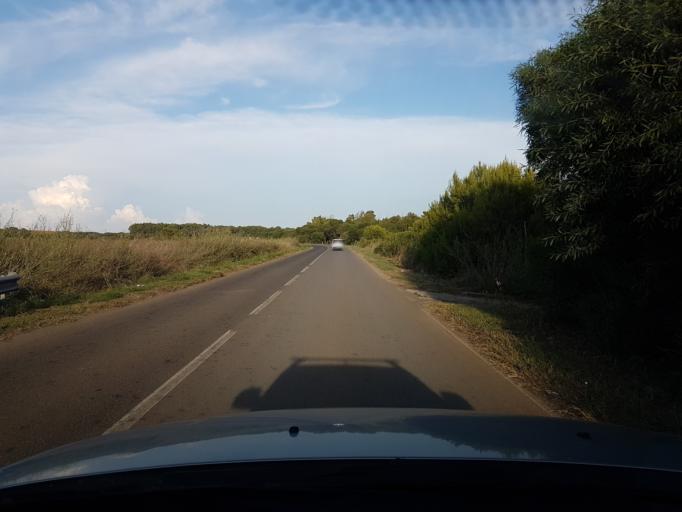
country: IT
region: Sardinia
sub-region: Provincia di Oristano
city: Cabras
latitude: 39.9503
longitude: 8.4210
